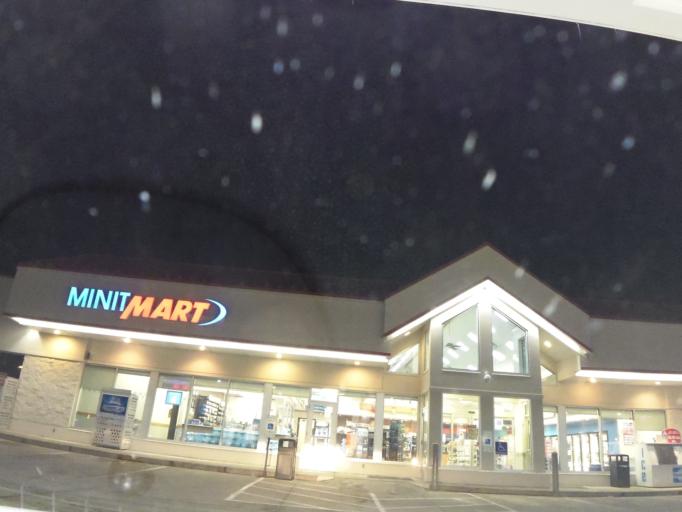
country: US
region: Illinois
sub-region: Champaign County
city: Mahomet
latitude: 40.1957
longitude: -88.3998
